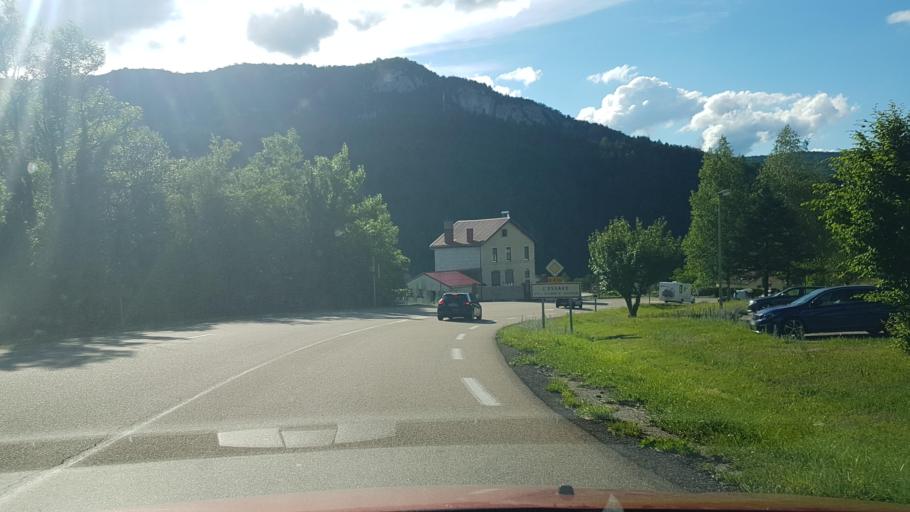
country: FR
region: Franche-Comte
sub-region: Departement du Jura
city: Saint-Claude
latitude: 46.3689
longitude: 5.8758
